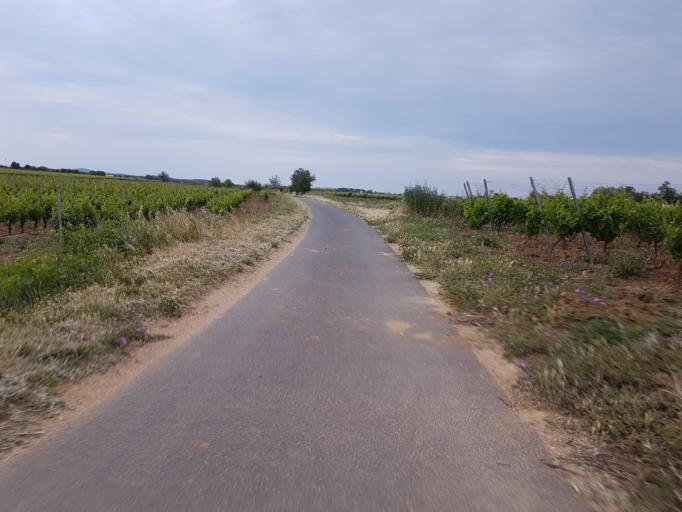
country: FR
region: Languedoc-Roussillon
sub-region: Departement de l'Herault
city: Cers
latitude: 43.3198
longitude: 3.3178
